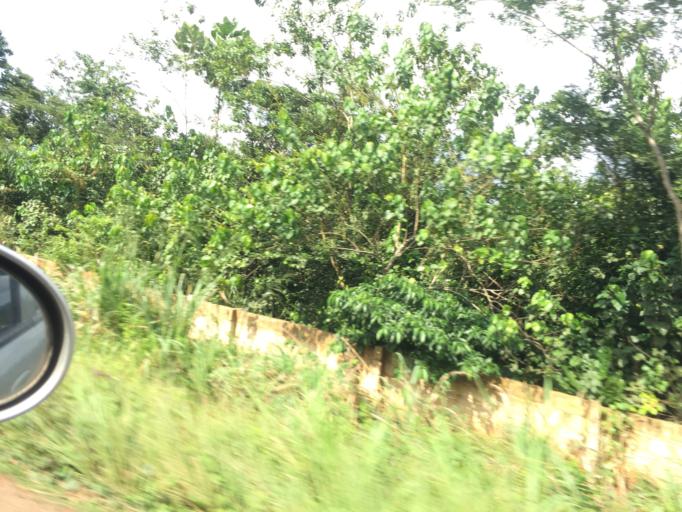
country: GH
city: Mpraeso
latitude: 6.6097
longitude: -0.7403
